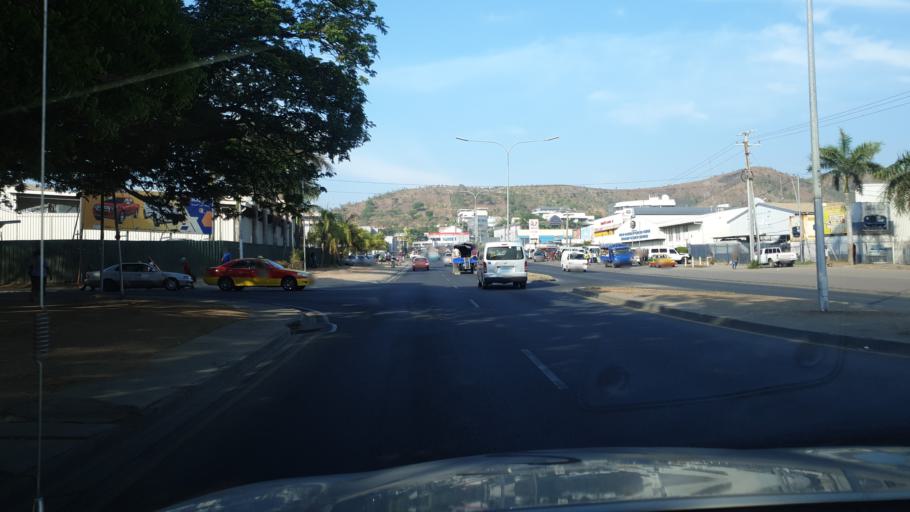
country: PG
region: National Capital
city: Port Moresby
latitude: -9.4434
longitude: 147.1857
